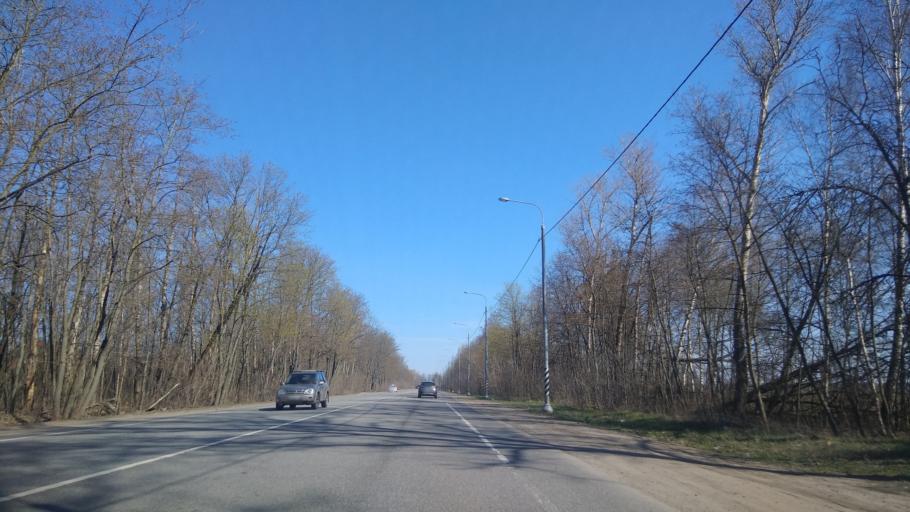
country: RU
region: Moskovskaya
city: Pushkino
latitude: 56.0347
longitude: 37.8706
